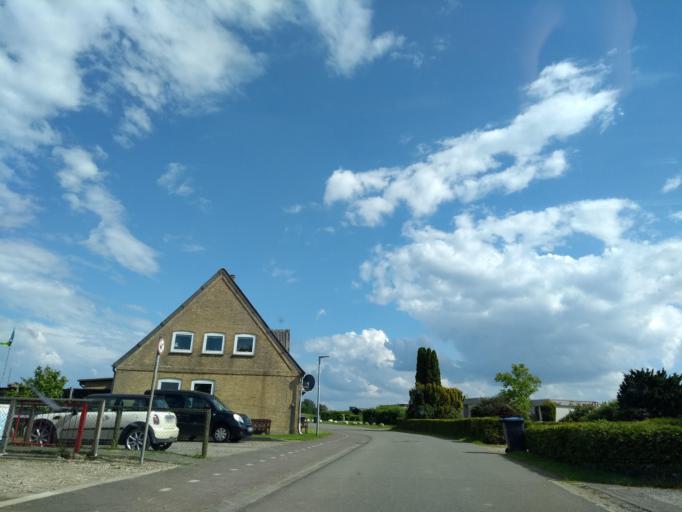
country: DE
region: Schleswig-Holstein
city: Thumby
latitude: 54.5573
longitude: 9.9230
